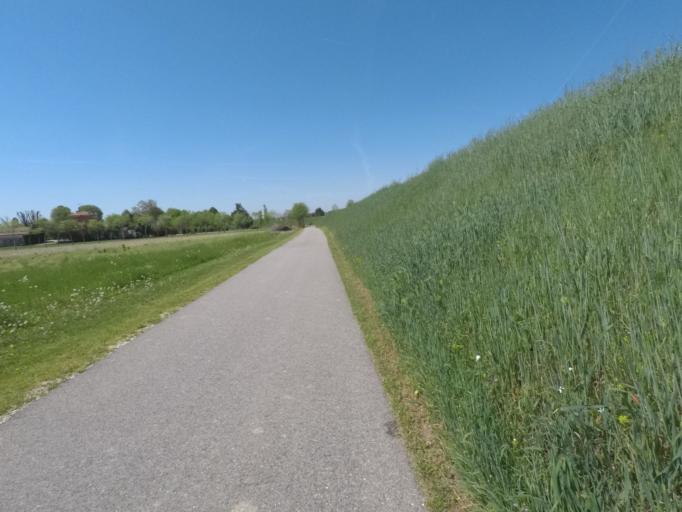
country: IT
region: Veneto
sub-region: Provincia di Treviso
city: Oderzo
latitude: 45.7872
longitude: 12.5108
